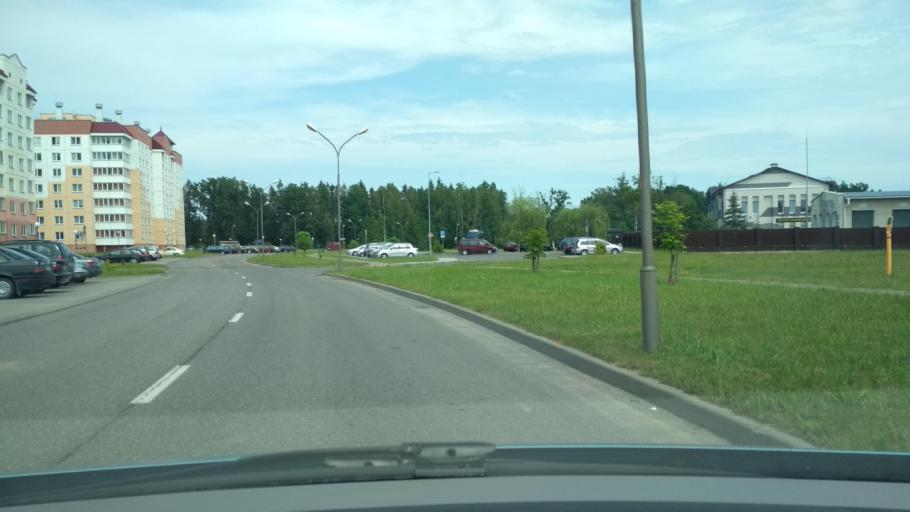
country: BY
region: Grodnenskaya
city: Astravyets
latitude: 54.6076
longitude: 25.9739
